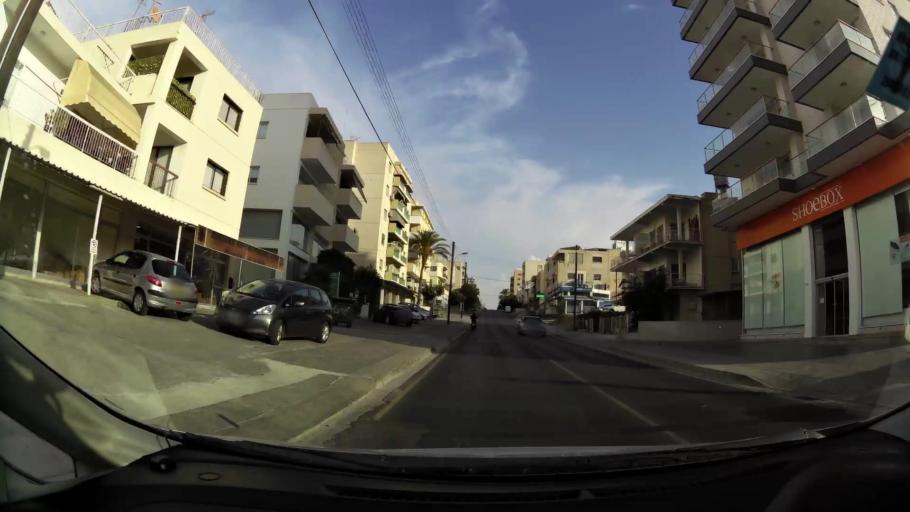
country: CY
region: Lefkosia
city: Nicosia
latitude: 35.1701
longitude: 33.3769
